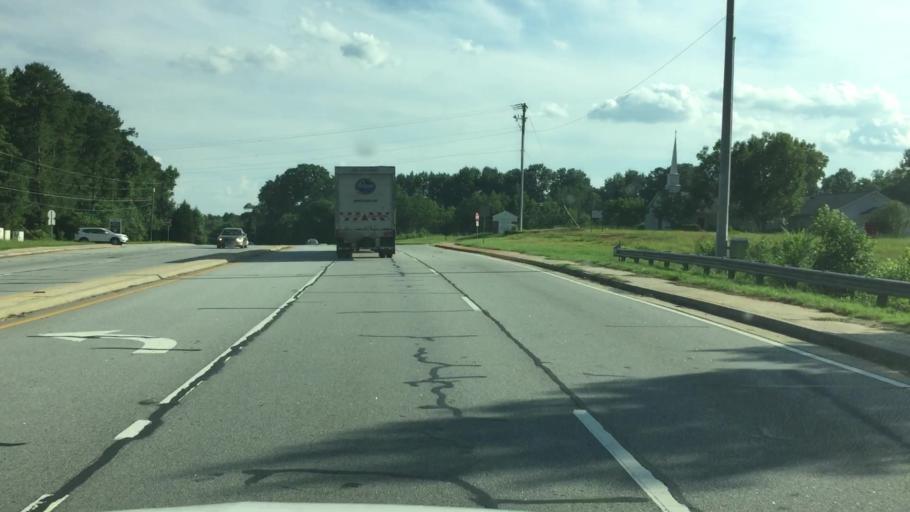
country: US
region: Georgia
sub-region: Gwinnett County
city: Snellville
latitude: 33.7880
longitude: -84.0459
